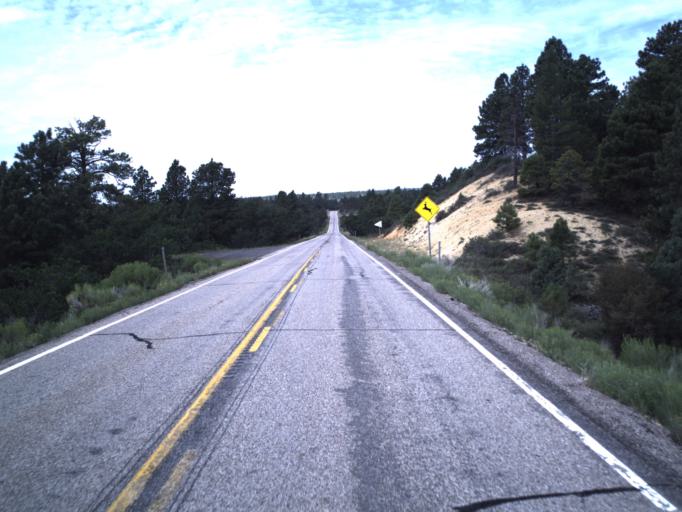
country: US
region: Utah
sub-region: Garfield County
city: Panguitch
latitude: 37.4957
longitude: -112.5514
